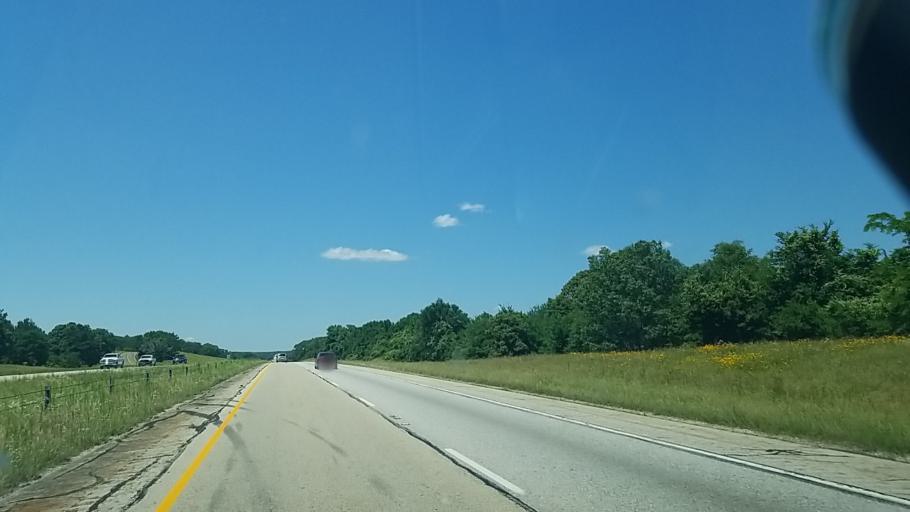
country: US
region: Texas
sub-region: Leon County
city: Centerville
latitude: 31.1632
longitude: -95.9861
